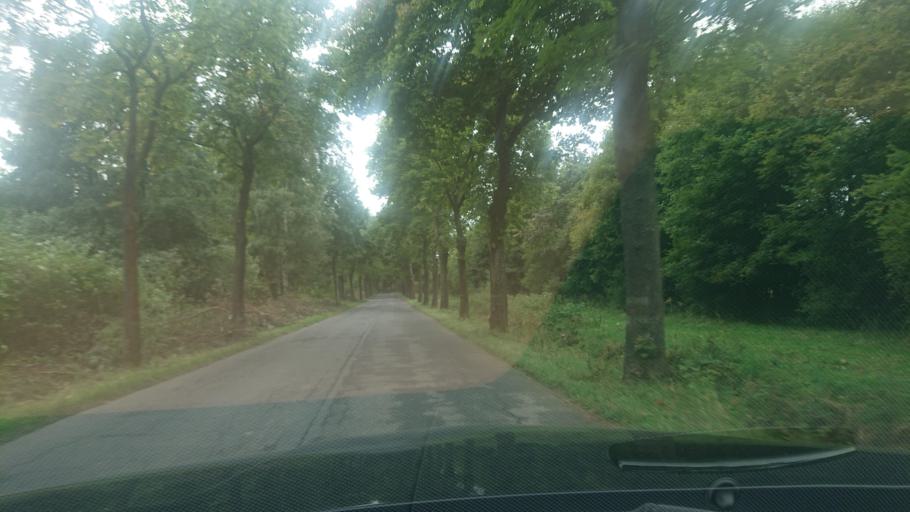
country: PL
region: Lower Silesian Voivodeship
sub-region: Powiat klodzki
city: Miedzylesie
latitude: 50.2206
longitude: 16.7109
